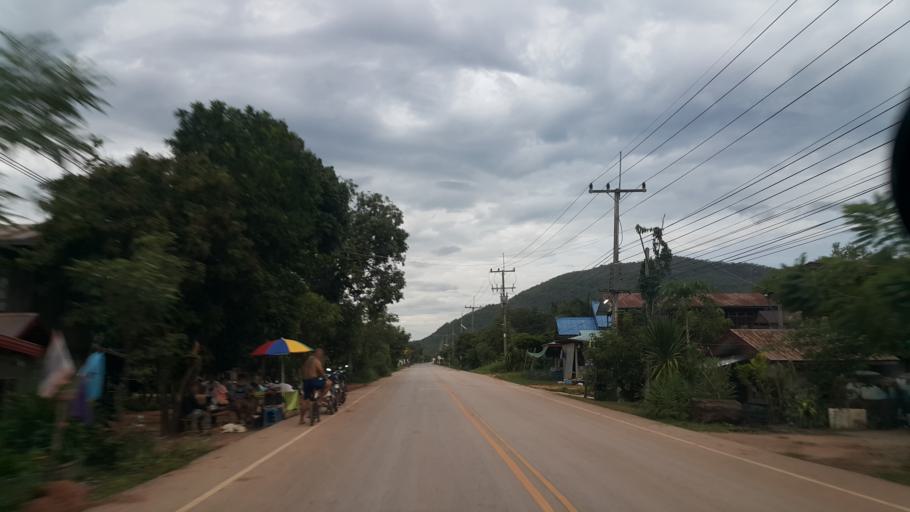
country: TH
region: Loei
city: Na Haeo
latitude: 17.5182
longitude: 101.1779
